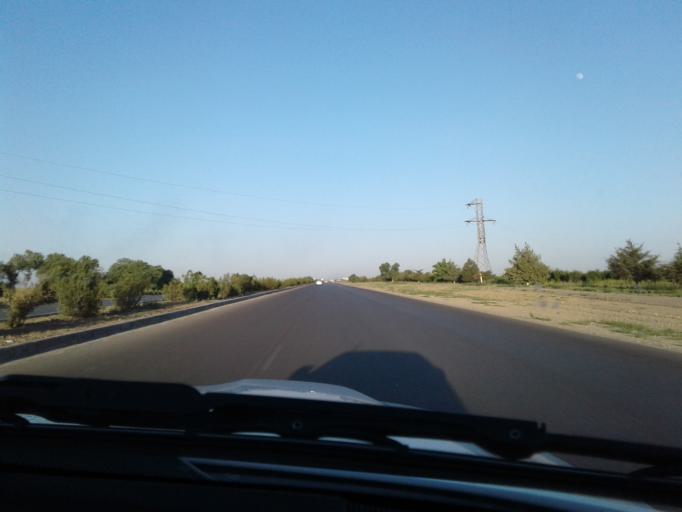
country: TM
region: Ahal
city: Arcabil
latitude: 38.1805
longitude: 57.8738
